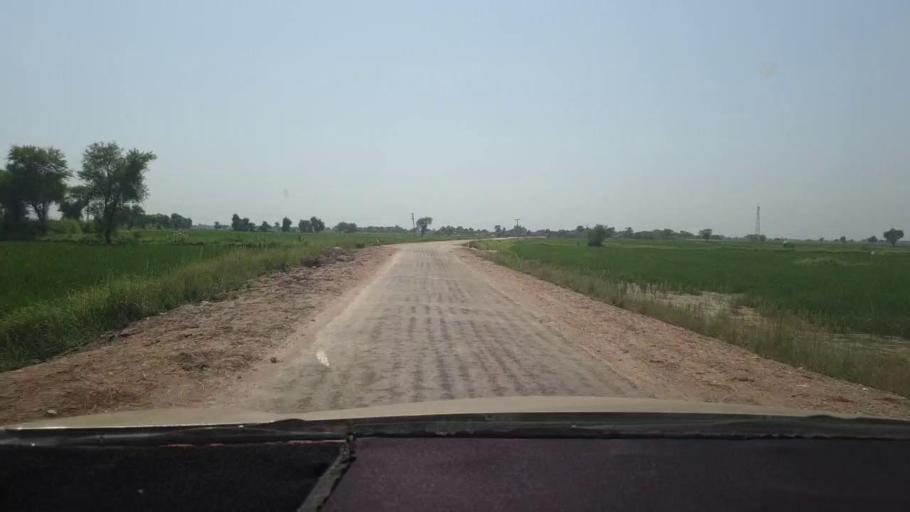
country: PK
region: Sindh
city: Miro Khan
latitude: 27.6638
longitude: 68.0887
